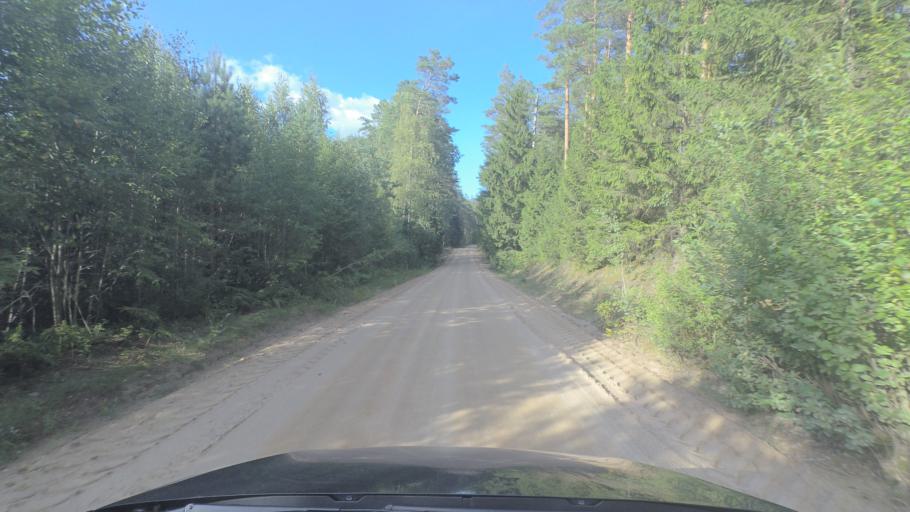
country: LT
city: Pabrade
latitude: 55.1634
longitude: 25.8287
